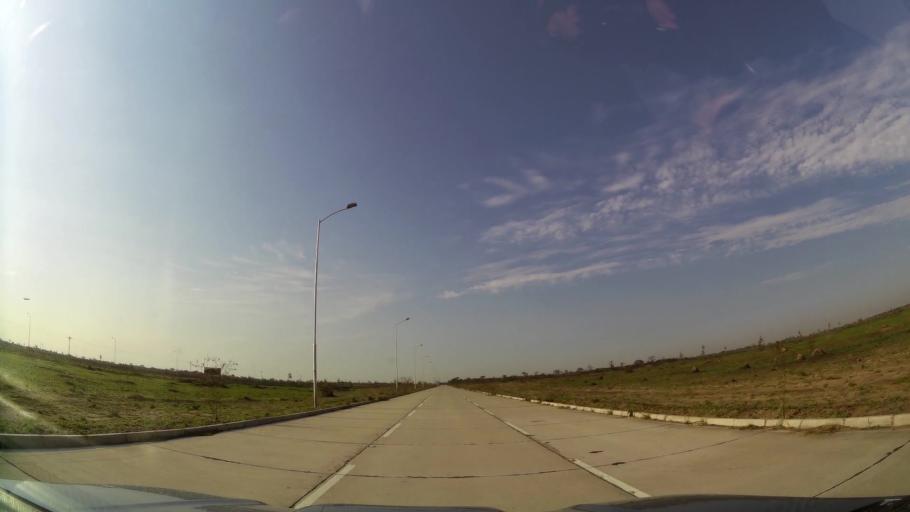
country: BO
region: Santa Cruz
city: Santa Cruz de la Sierra
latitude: -17.6610
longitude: -63.1351
